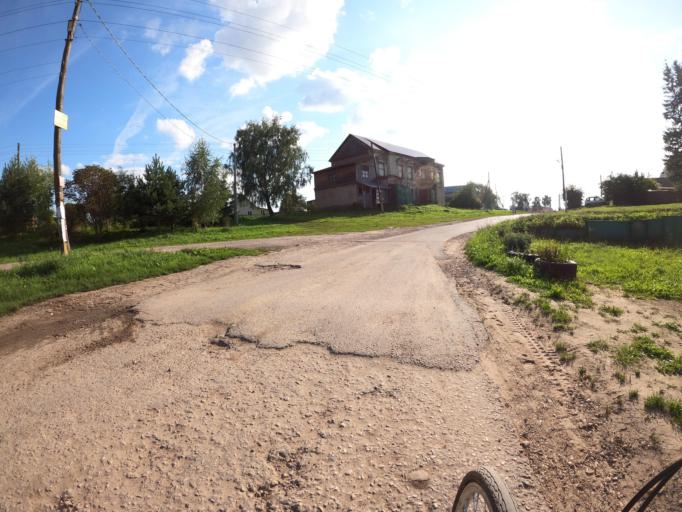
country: RU
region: Moskovskaya
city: Troitskoye
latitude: 55.1930
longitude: 38.4893
